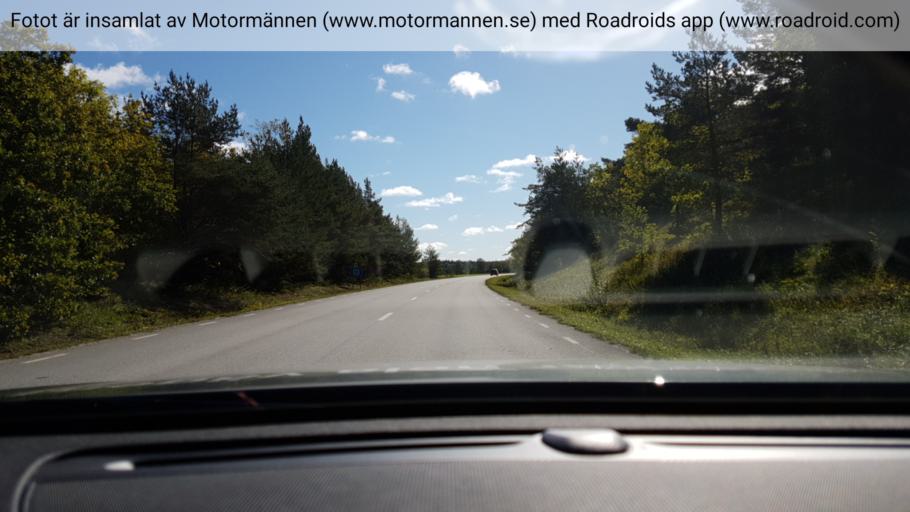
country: SE
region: Gotland
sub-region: Gotland
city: Slite
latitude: 57.7700
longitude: 18.7860
